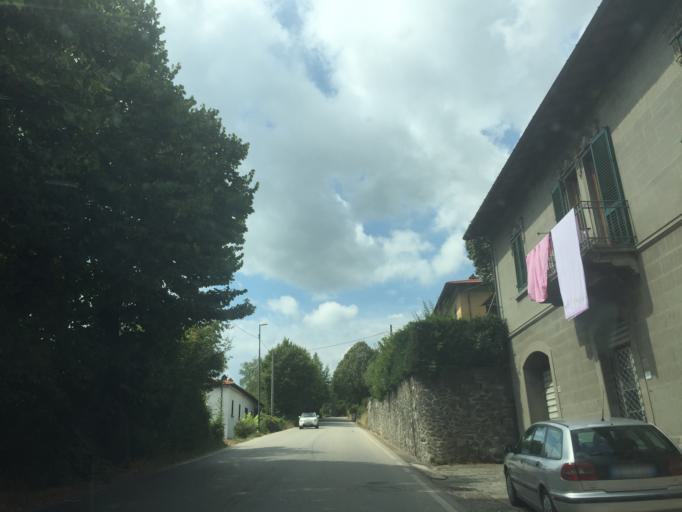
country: IT
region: Tuscany
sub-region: Provincia di Pistoia
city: Campo Tizzoro
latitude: 44.0381
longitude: 10.8497
